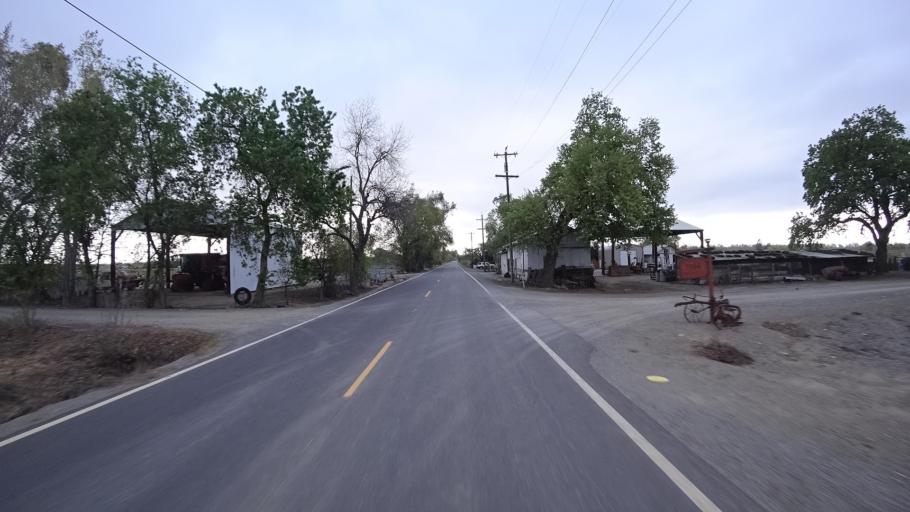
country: US
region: California
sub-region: Colusa County
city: Colusa
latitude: 39.4063
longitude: -122.0219
